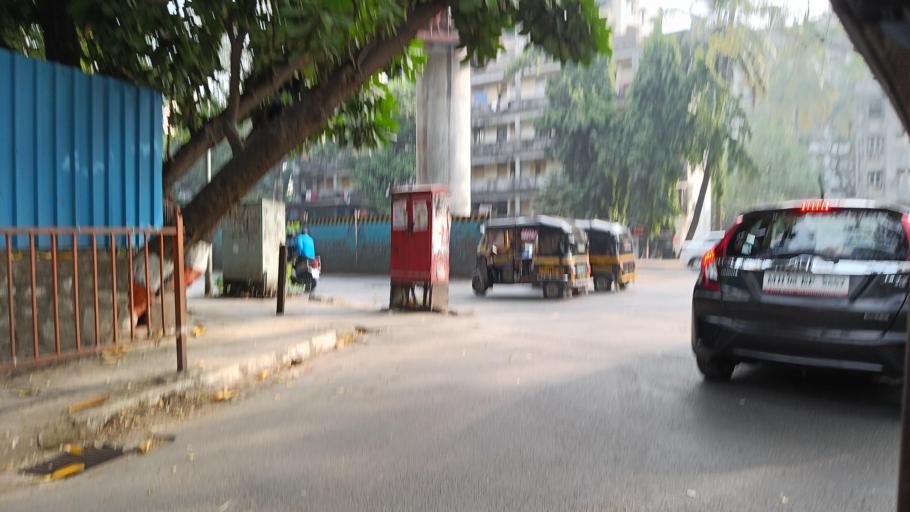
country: IN
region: Maharashtra
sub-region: Mumbai Suburban
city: Mumbai
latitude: 19.1233
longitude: 72.8300
